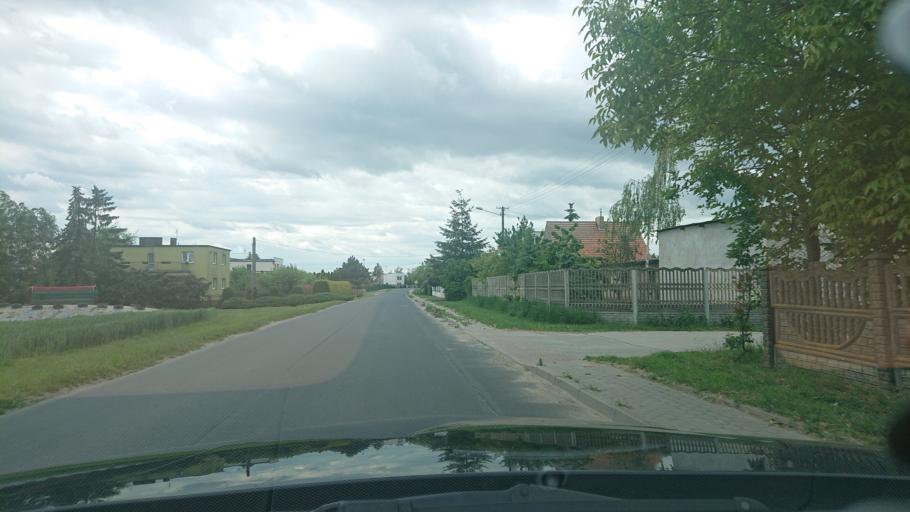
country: PL
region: Greater Poland Voivodeship
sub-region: Powiat gnieznienski
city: Gniezno
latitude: 52.5405
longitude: 17.5498
